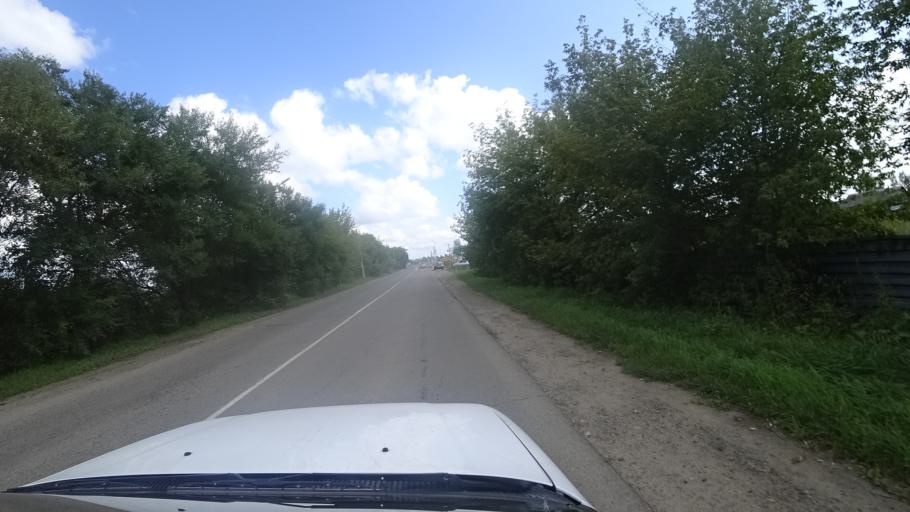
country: RU
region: Primorskiy
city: Dal'nerechensk
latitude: 45.9256
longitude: 133.7703
